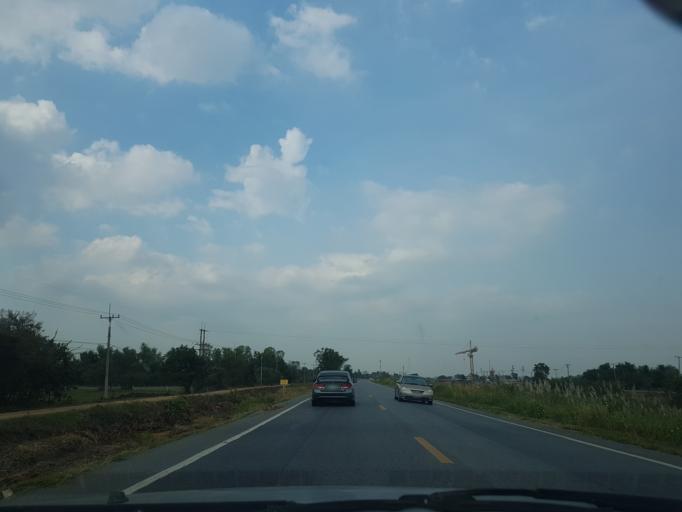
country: TH
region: Phra Nakhon Si Ayutthaya
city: Phachi
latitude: 14.4946
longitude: 100.7357
